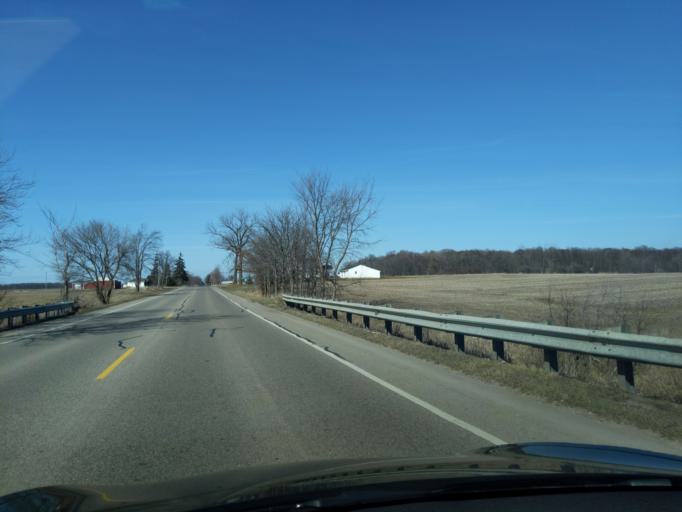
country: US
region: Michigan
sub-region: Ionia County
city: Lake Odessa
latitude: 42.7975
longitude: -85.1334
